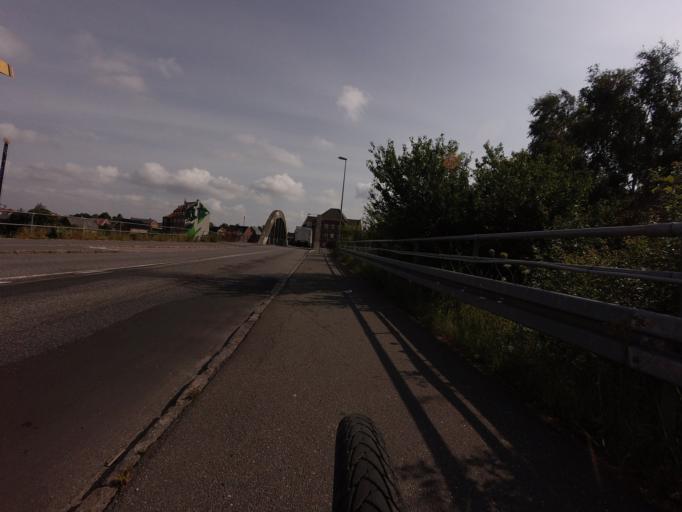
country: DK
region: Zealand
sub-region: Naestved Kommune
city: Naestved
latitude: 55.2286
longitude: 11.7695
